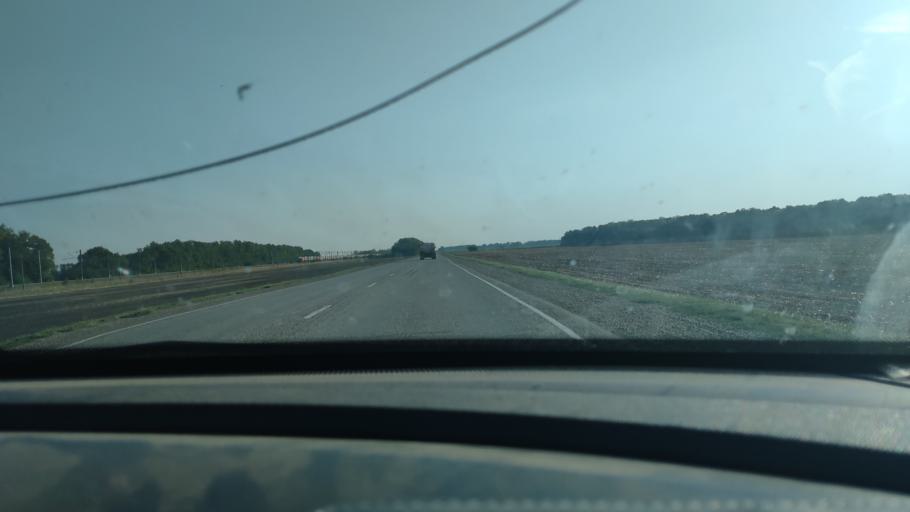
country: RU
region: Krasnodarskiy
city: Starominskaya
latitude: 46.4732
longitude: 39.0460
